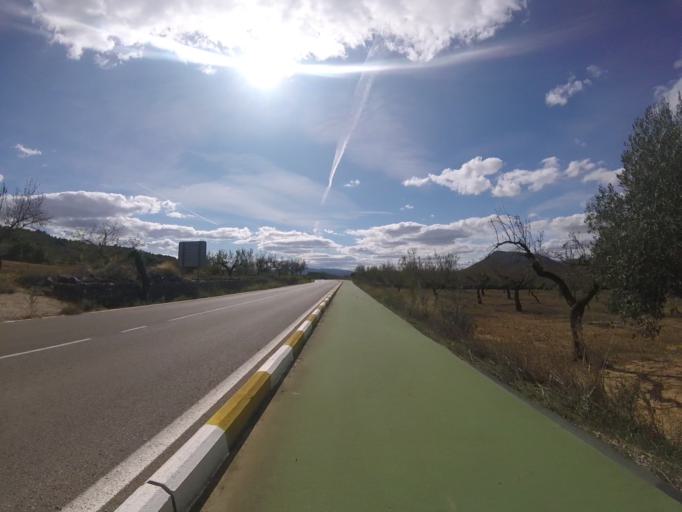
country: ES
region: Valencia
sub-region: Provincia de Castello
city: Cati
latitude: 40.4206
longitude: 0.0733
